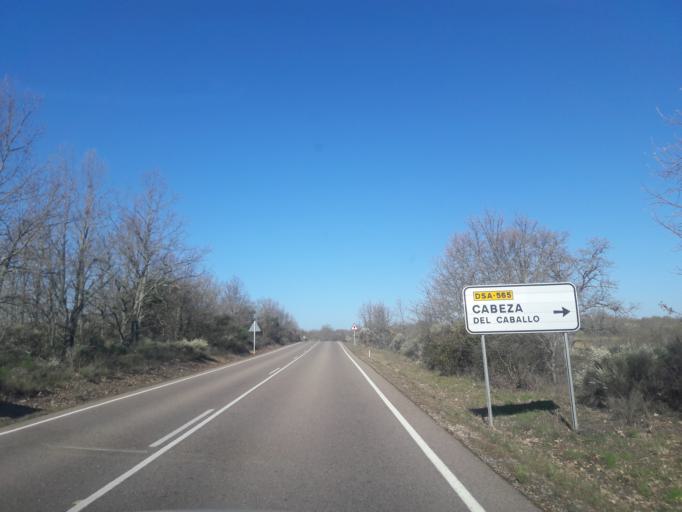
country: ES
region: Castille and Leon
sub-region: Provincia de Salamanca
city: Villasbuenas
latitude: 41.0794
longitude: -6.5601
